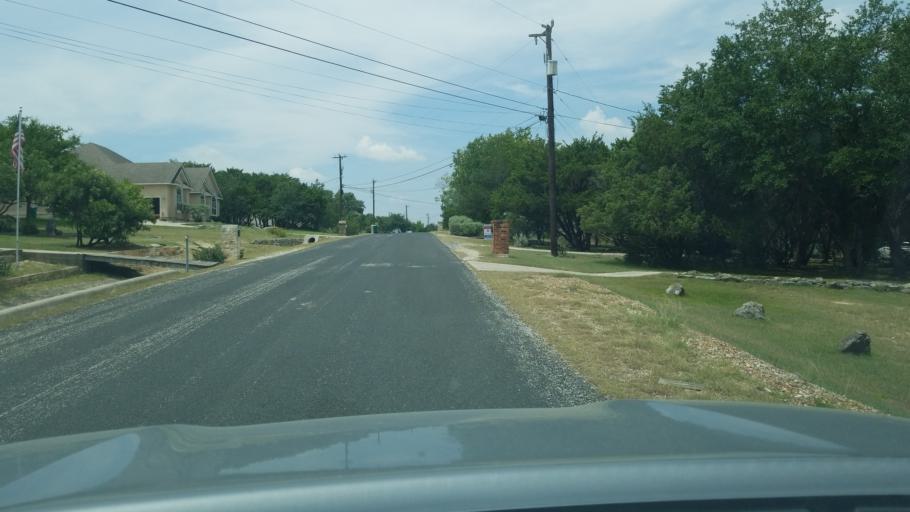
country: US
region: Texas
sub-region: Bexar County
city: Timberwood Park
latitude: 29.6886
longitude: -98.5045
